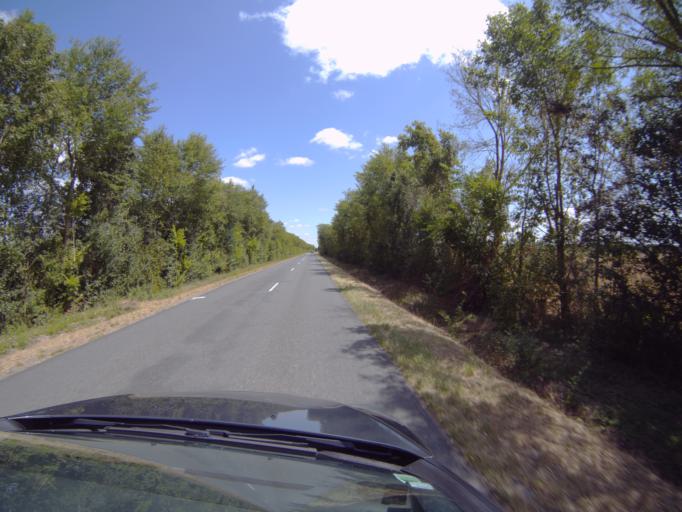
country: FR
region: Poitou-Charentes
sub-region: Departement de la Charente-Maritime
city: Saint-Jean-de-Liversay
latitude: 46.2568
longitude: -0.8473
